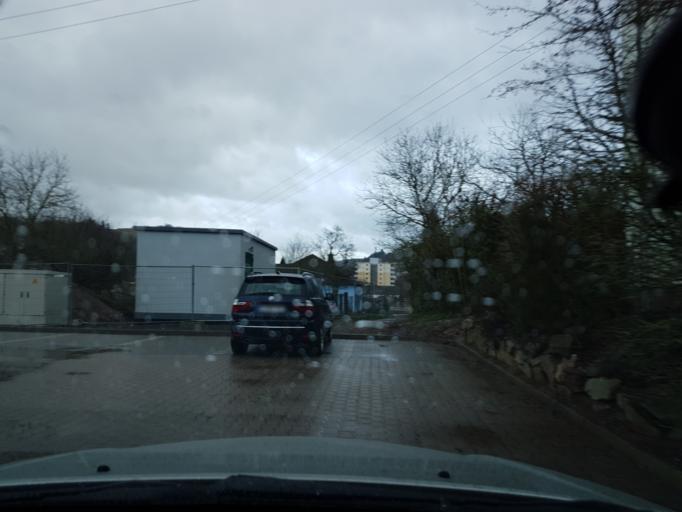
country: DE
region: Rheinland-Pfalz
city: Hintertiefenbach
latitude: 49.7162
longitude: 7.3652
